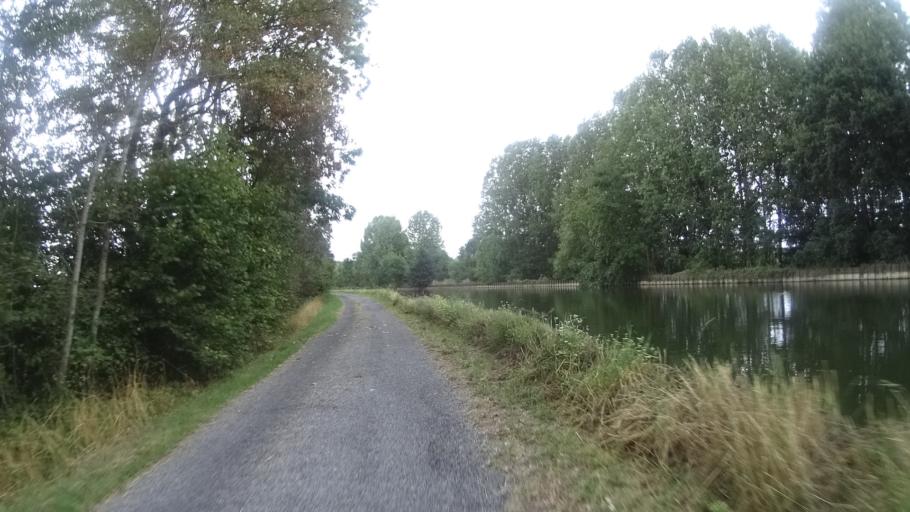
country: FR
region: Picardie
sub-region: Departement de l'Aisne
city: Ribemont
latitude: 49.8102
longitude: 3.4583
